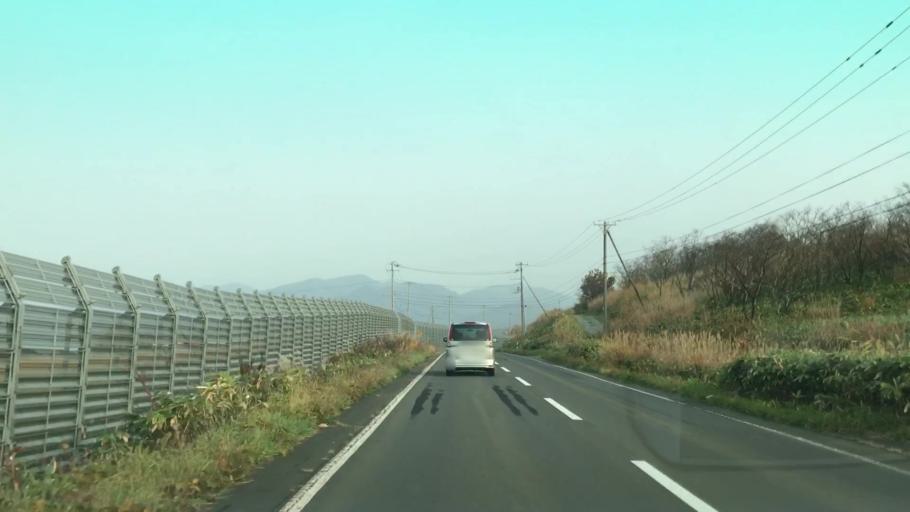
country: JP
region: Hokkaido
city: Ishikari
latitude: 43.3782
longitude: 141.4286
